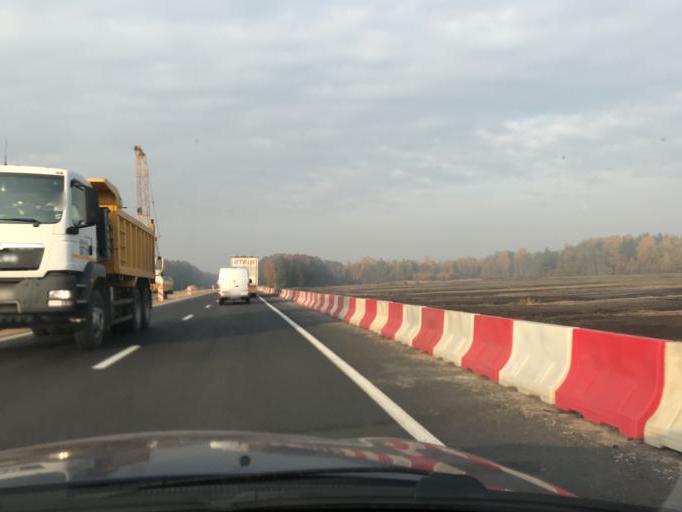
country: BY
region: Grodnenskaya
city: Lida
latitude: 53.8287
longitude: 25.4203
